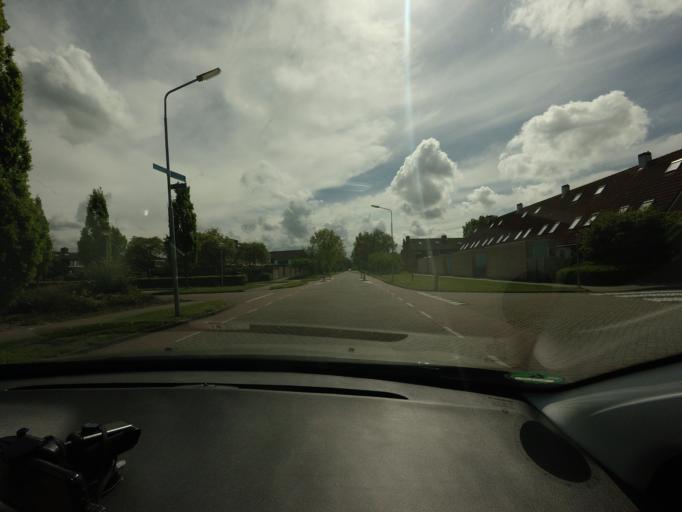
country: NL
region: North Holland
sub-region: Gemeente Beemster
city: Halfweg
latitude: 52.5579
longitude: 4.8434
